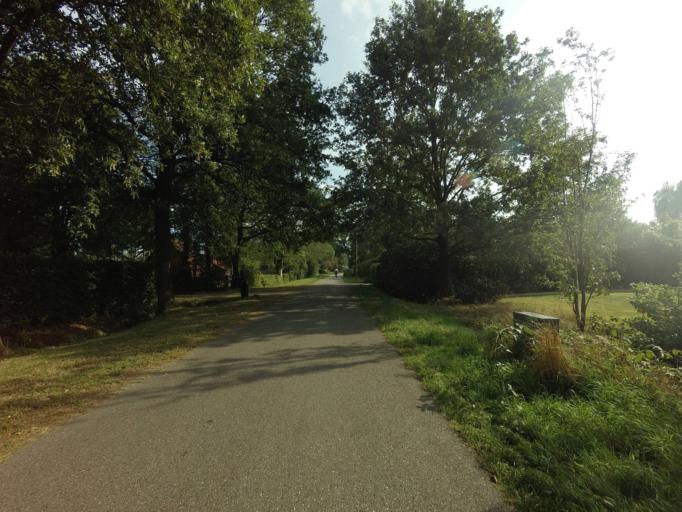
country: NL
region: Drenthe
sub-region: Gemeente Tynaarlo
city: Vries
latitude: 53.1200
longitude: 6.5698
